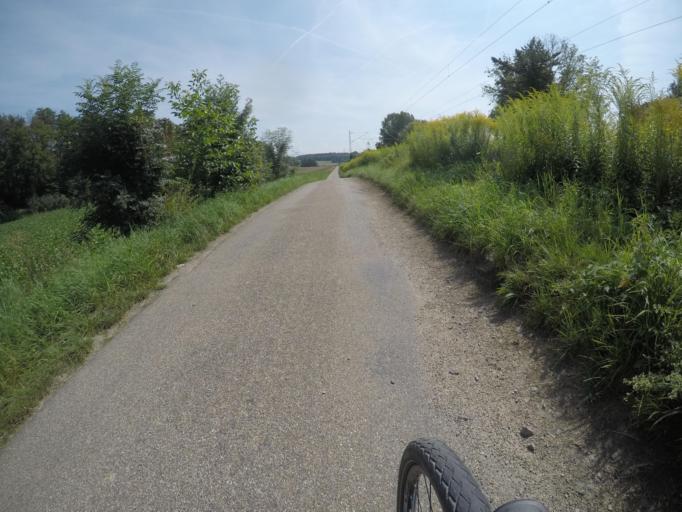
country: DE
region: Baden-Wuerttemberg
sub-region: Karlsruhe Region
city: Gondelsheim
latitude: 49.0772
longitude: 8.6565
